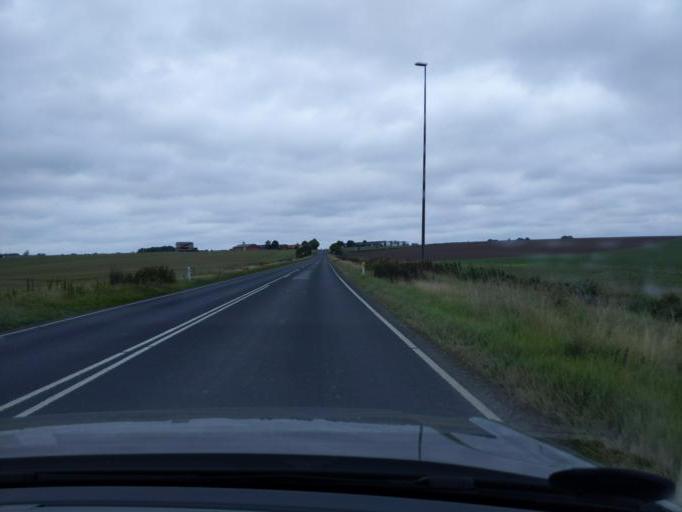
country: DK
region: Central Jutland
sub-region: Randers Kommune
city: Spentrup
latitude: 56.5185
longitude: 9.9413
